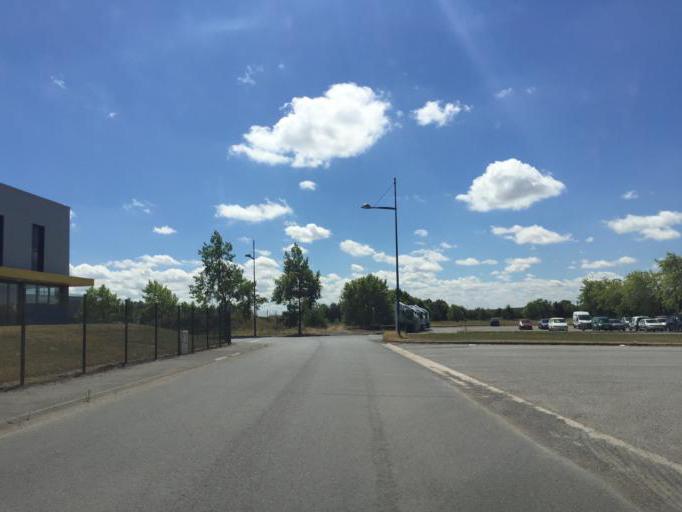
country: FR
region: Auvergne
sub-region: Departement de l'Allier
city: Avermes
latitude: 46.5940
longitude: 3.3288
